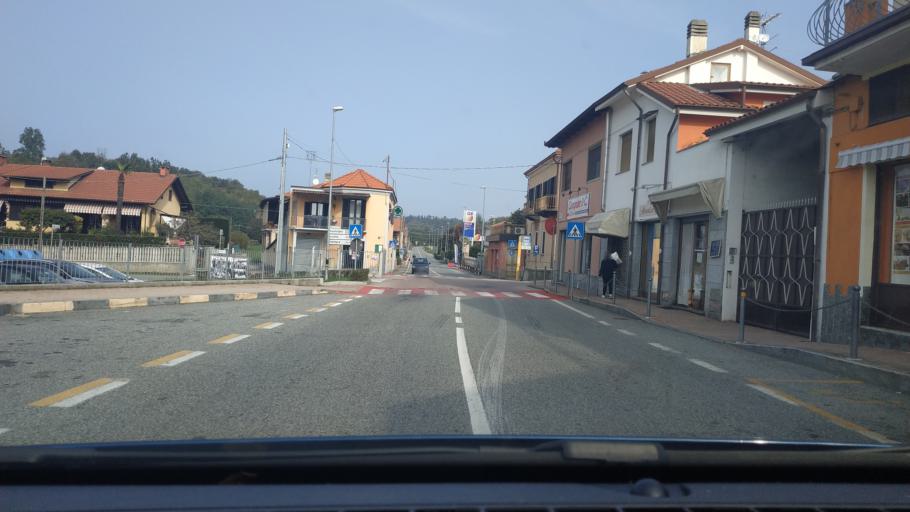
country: IT
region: Piedmont
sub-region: Provincia di Torino
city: Montalenghe
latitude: 45.3367
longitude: 7.8354
